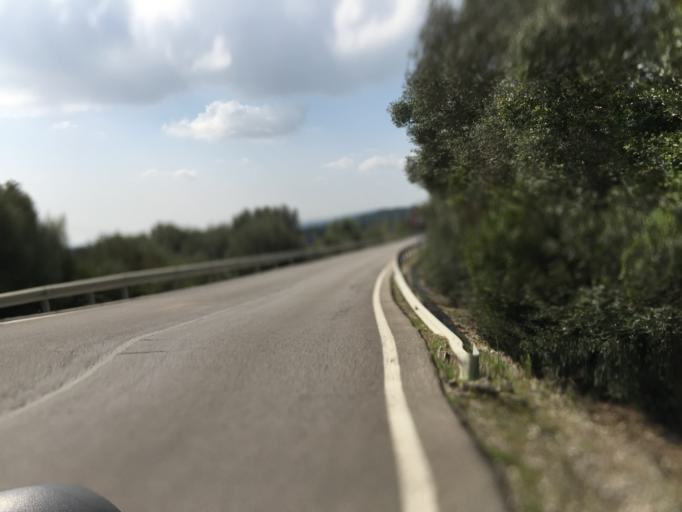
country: ES
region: Andalusia
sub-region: Provincia de Cadiz
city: Vejer de la Frontera
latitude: 36.2883
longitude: -5.9335
